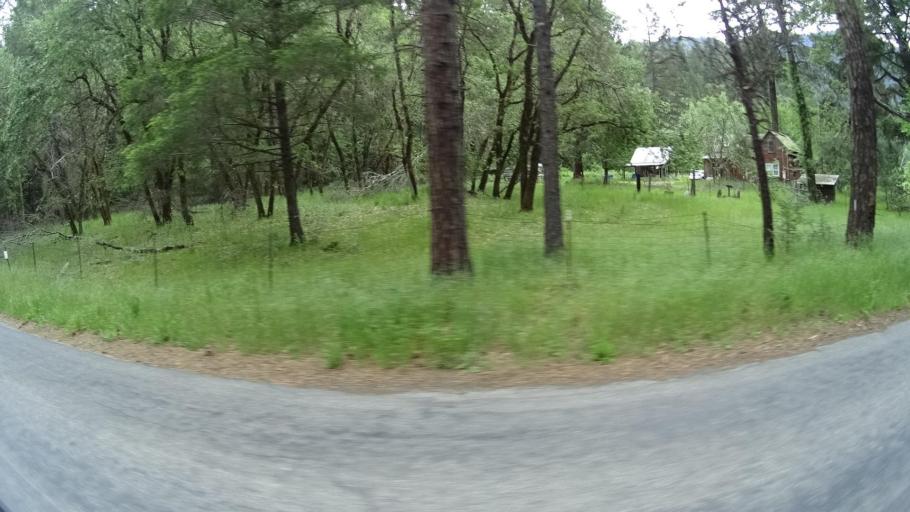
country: US
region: California
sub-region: Humboldt County
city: Willow Creek
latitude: 40.9644
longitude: -123.6330
